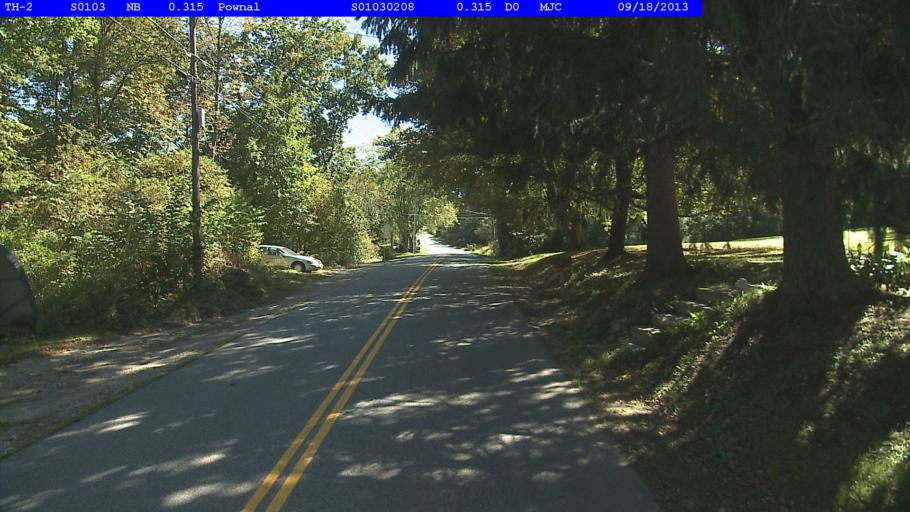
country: US
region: Vermont
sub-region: Bennington County
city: Bennington
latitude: 42.8067
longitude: -73.2616
